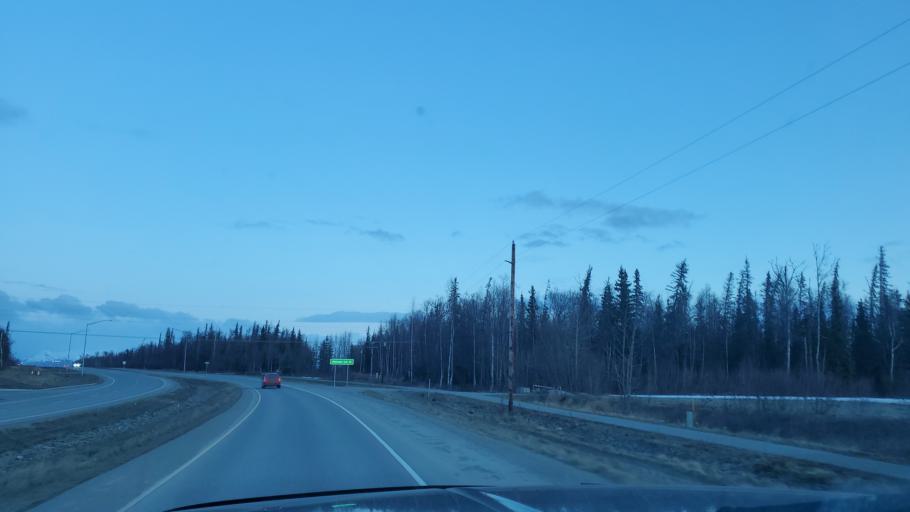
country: US
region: Alaska
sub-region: Matanuska-Susitna Borough
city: Wasilla
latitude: 61.5705
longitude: -149.4387
